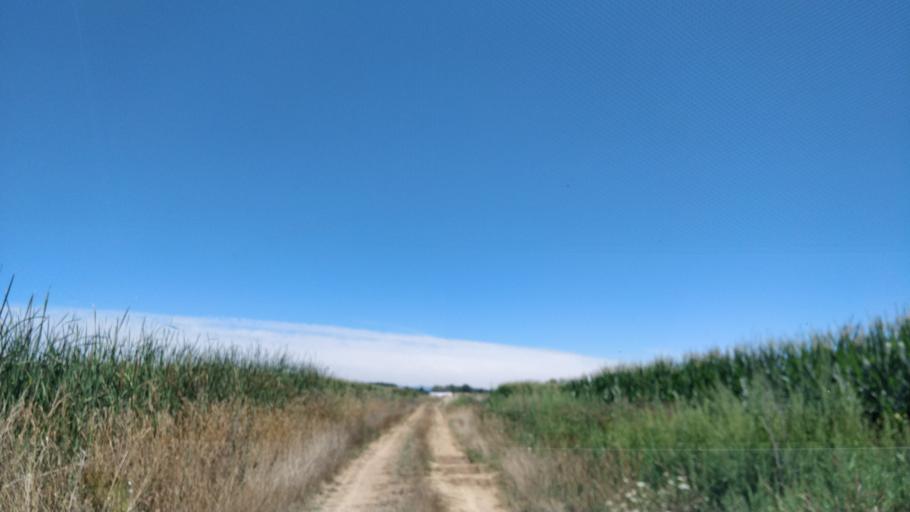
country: ES
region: Castille and Leon
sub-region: Provincia de Leon
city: Bustillo del Paramo
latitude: 42.4688
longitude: -5.8137
